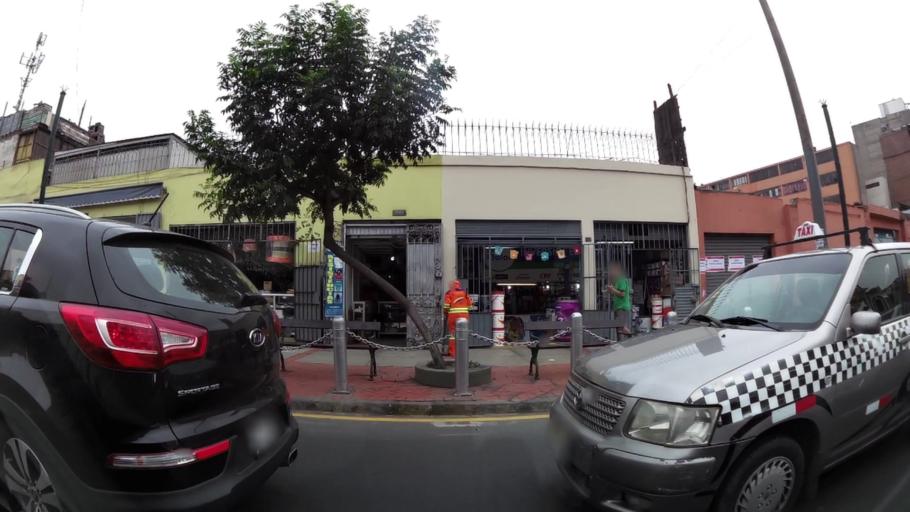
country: PE
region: Lima
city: Lima
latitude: -12.0542
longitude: -77.0340
